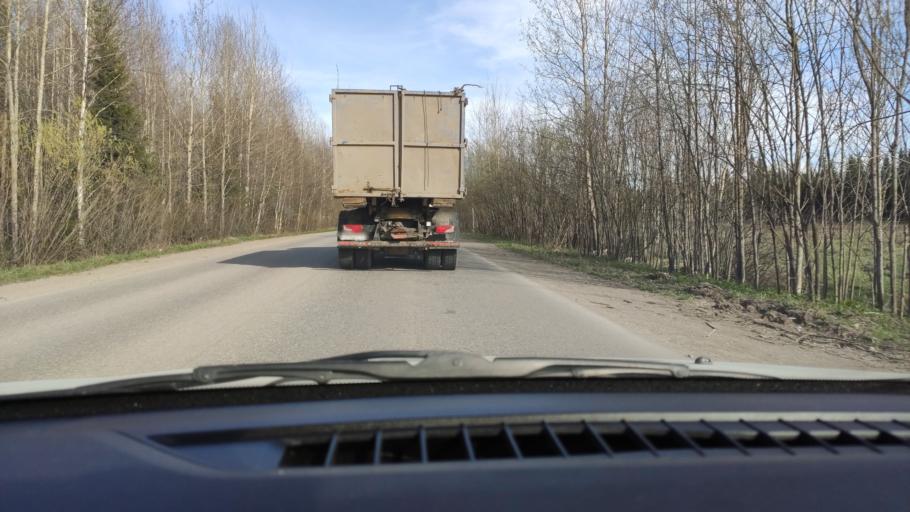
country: RU
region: Perm
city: Ferma
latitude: 57.9355
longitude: 56.4717
